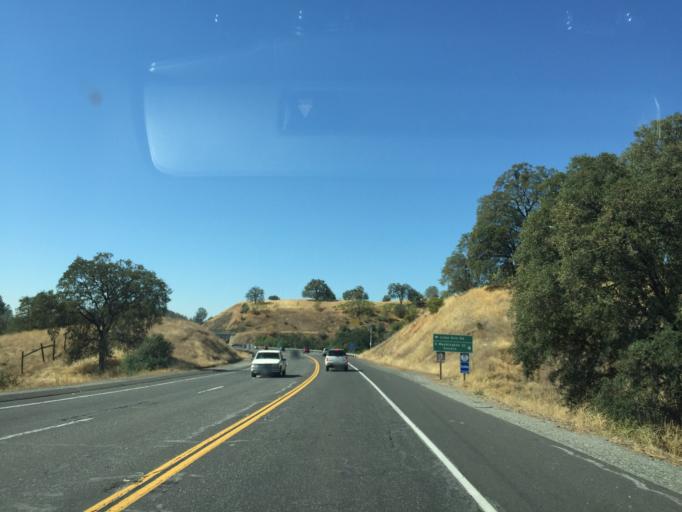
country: US
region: California
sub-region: Tuolumne County
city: East Sonora
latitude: 37.9693
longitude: -120.3743
